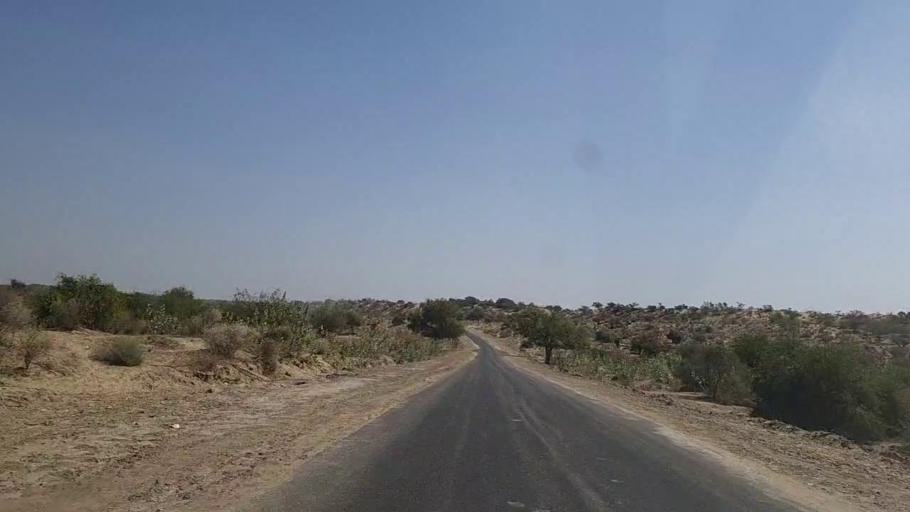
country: PK
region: Sindh
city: Diplo
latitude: 24.4813
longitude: 69.4831
